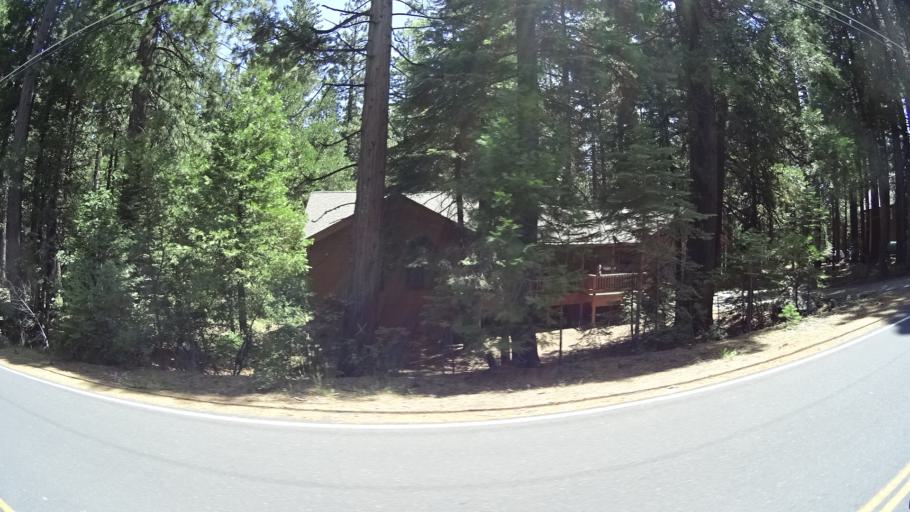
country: US
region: California
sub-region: Calaveras County
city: Arnold
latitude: 38.3183
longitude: -120.2521
